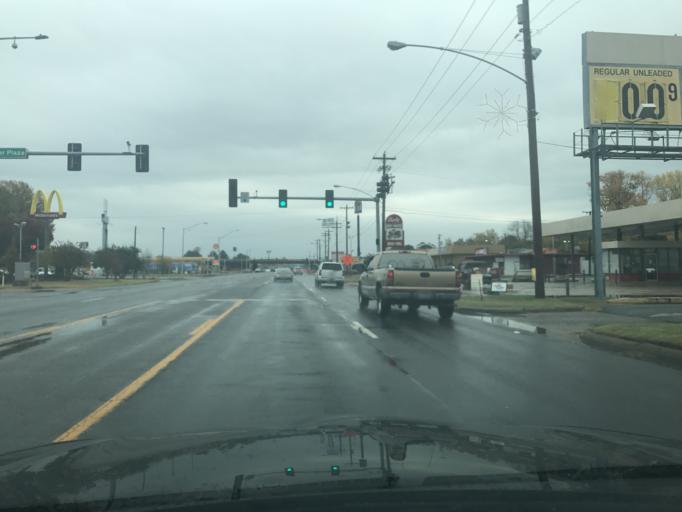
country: US
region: Arkansas
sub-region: Faulkner County
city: Conway
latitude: 35.0916
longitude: -92.4274
